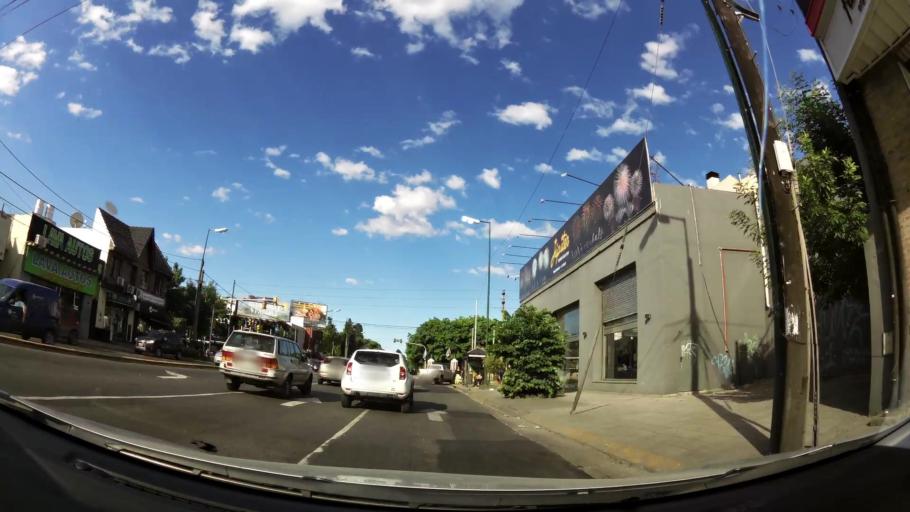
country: AR
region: Buenos Aires
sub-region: Partido de San Isidro
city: San Isidro
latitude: -34.4925
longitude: -58.5475
